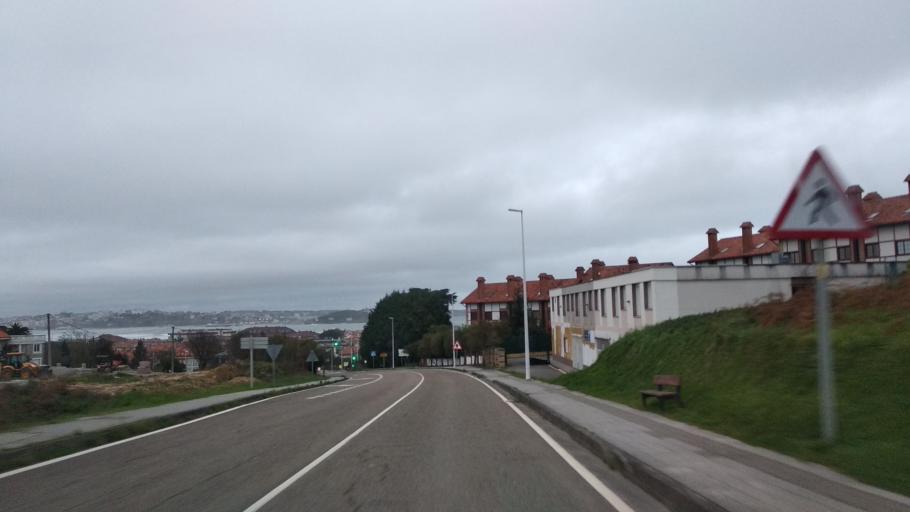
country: ES
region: Cantabria
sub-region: Provincia de Cantabria
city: Santander
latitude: 43.4524
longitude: -3.7392
